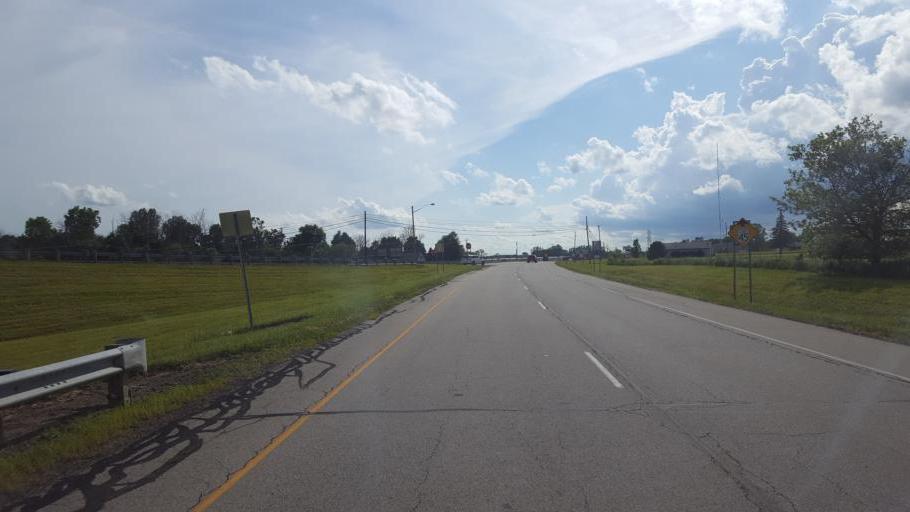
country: US
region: Ohio
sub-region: Richland County
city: Ontario
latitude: 40.7611
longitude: -82.6104
